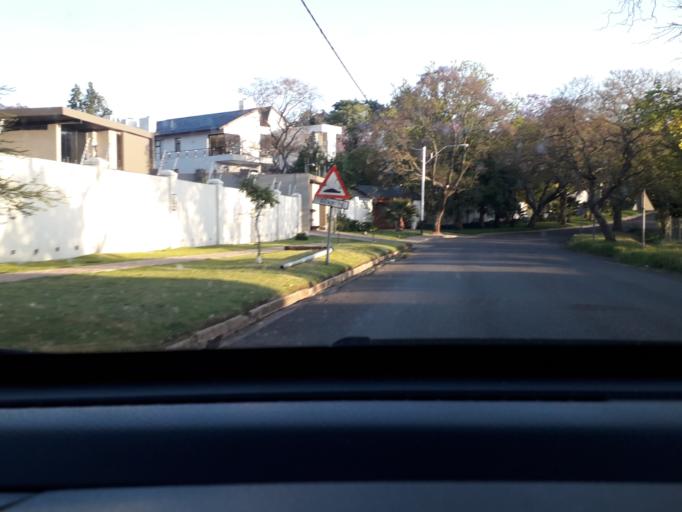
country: ZA
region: Gauteng
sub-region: City of Johannesburg Metropolitan Municipality
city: Johannesburg
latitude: -26.1442
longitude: 28.0502
